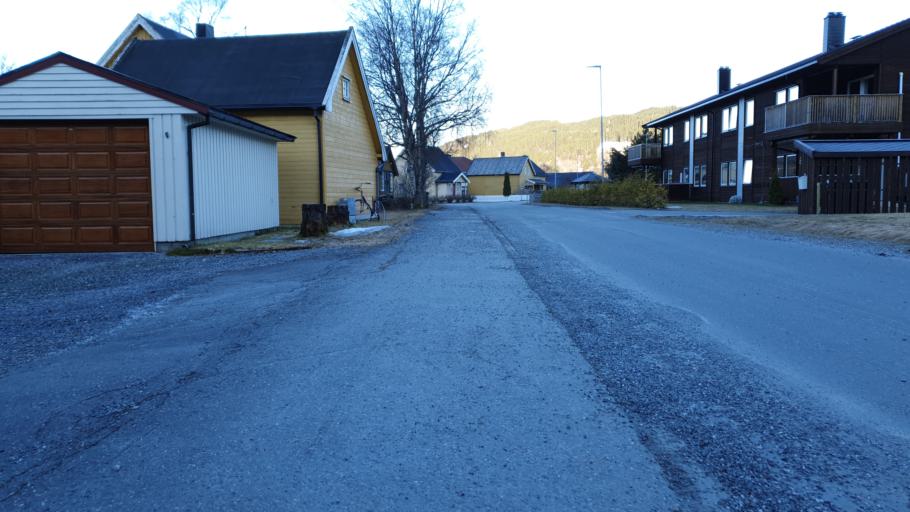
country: NO
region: Sor-Trondelag
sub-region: Orkdal
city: Orkanger
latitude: 63.2933
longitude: 9.8491
